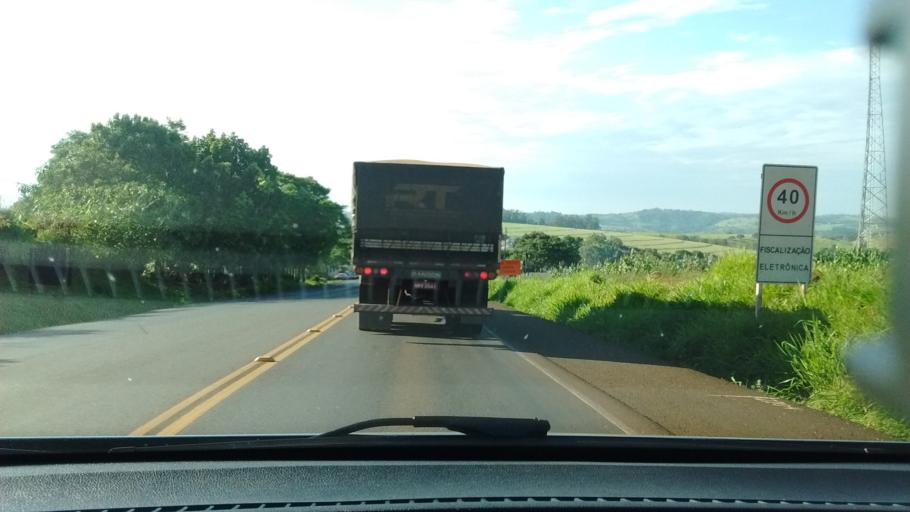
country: BR
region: Parana
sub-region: Cascavel
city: Cascavel
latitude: -25.2538
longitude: -53.5774
